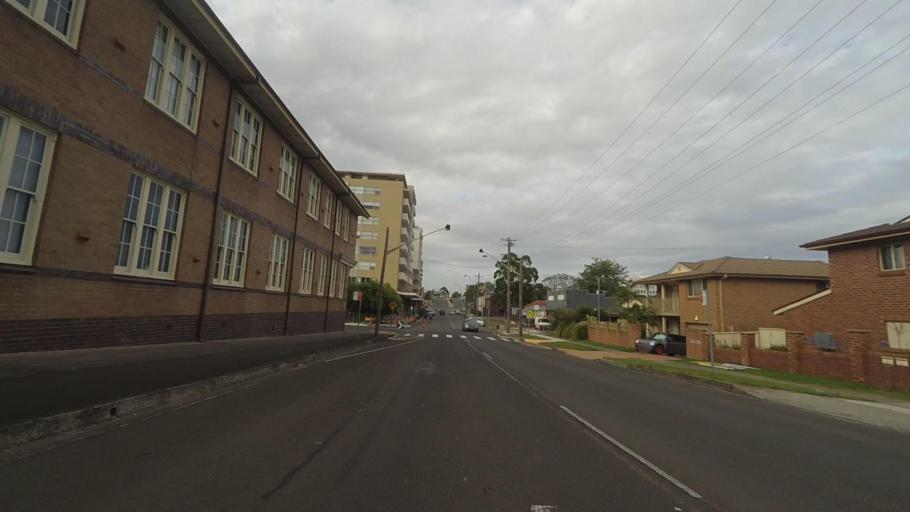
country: AU
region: New South Wales
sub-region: Wollongong
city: Wollongong
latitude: -34.4292
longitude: 150.8866
